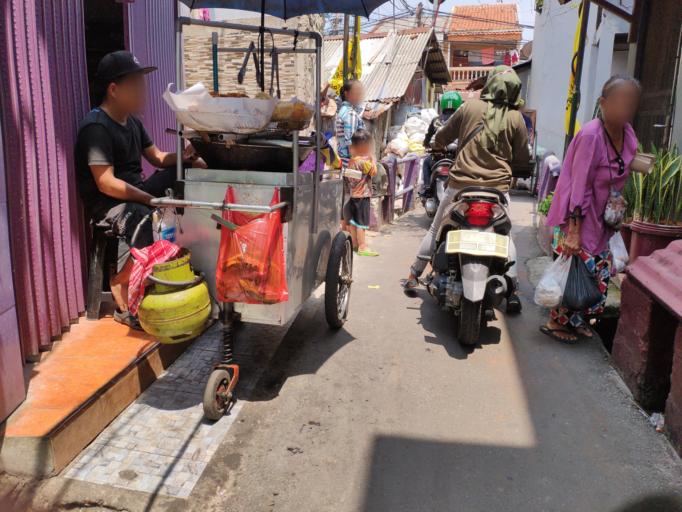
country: ID
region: Jakarta Raya
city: Jakarta
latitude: -6.2116
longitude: 106.8671
